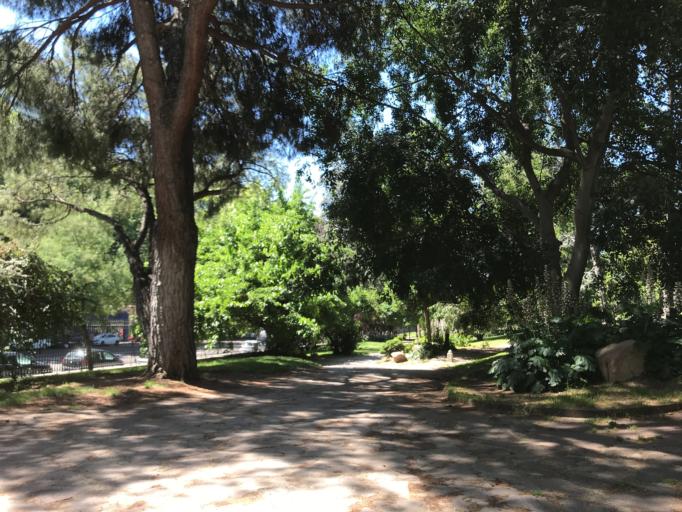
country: ES
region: Madrid
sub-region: Provincia de Madrid
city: Retiro
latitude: 40.4111
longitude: -3.6768
